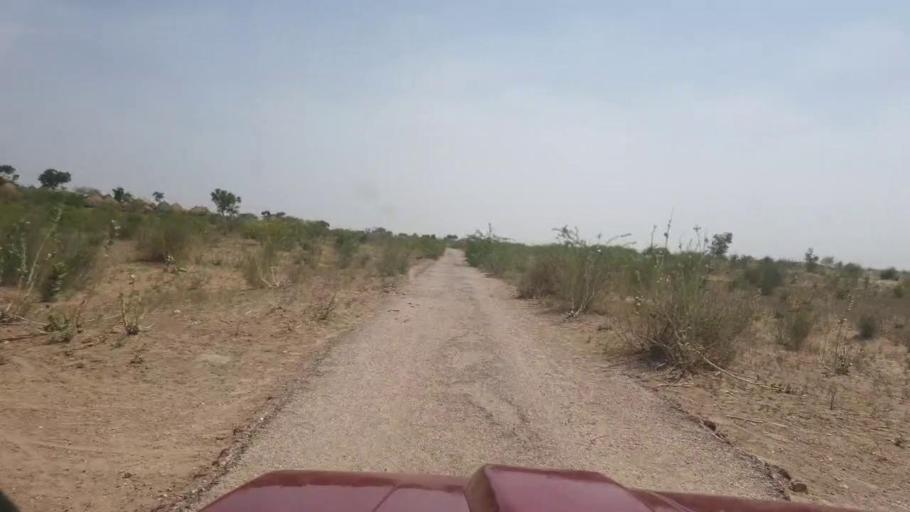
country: PK
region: Sindh
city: Islamkot
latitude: 25.1162
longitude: 70.3762
